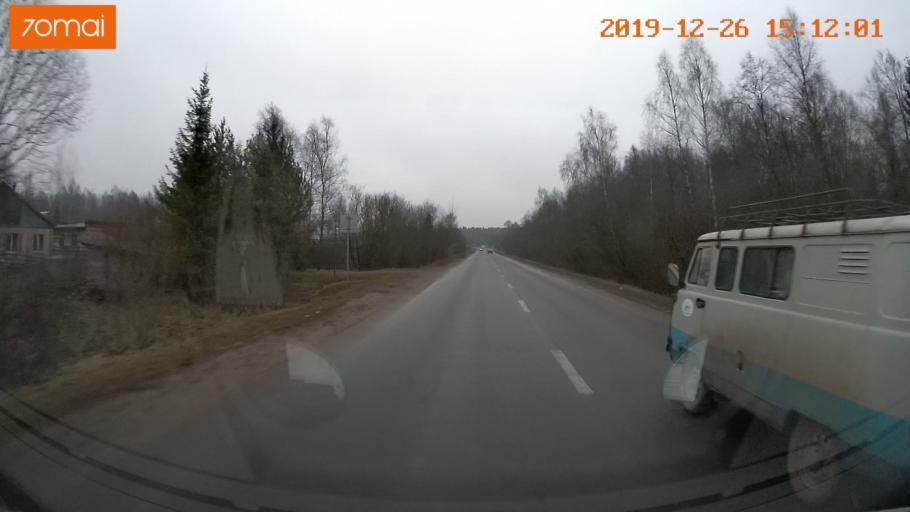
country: RU
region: Jaroslavl
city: Rybinsk
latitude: 58.1314
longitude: 38.8695
